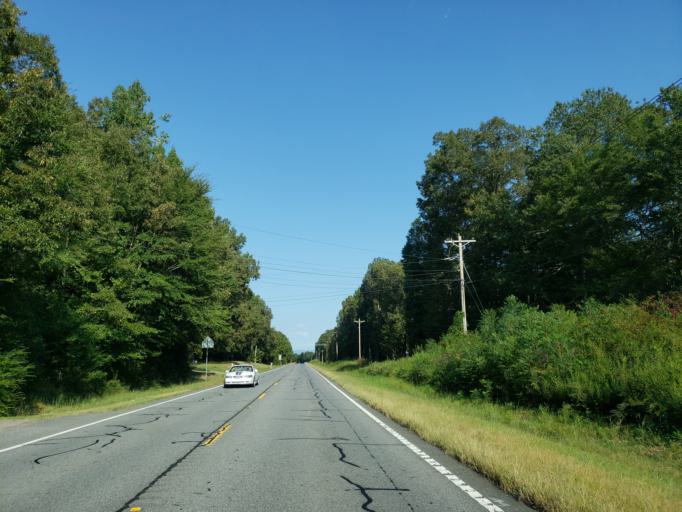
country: US
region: Georgia
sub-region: Whitfield County
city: Varnell
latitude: 34.8948
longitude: -84.9389
